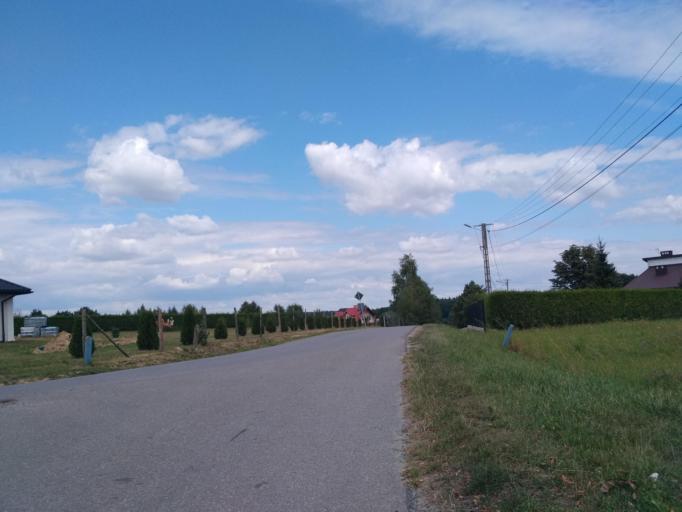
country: PL
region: Subcarpathian Voivodeship
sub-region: Powiat rzeszowski
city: Hyzne
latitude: 49.9174
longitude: 22.2116
